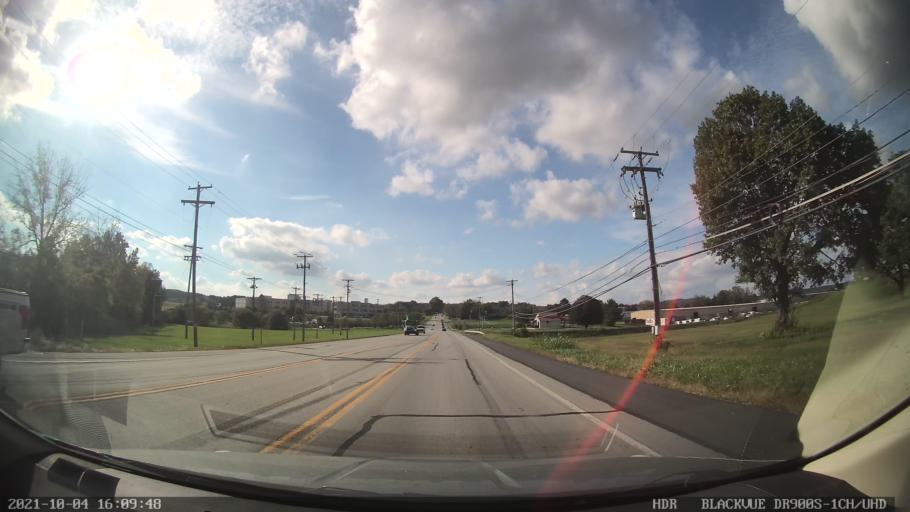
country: US
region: Pennsylvania
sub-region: Berks County
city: River View Park
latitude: 40.3750
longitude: -75.9723
